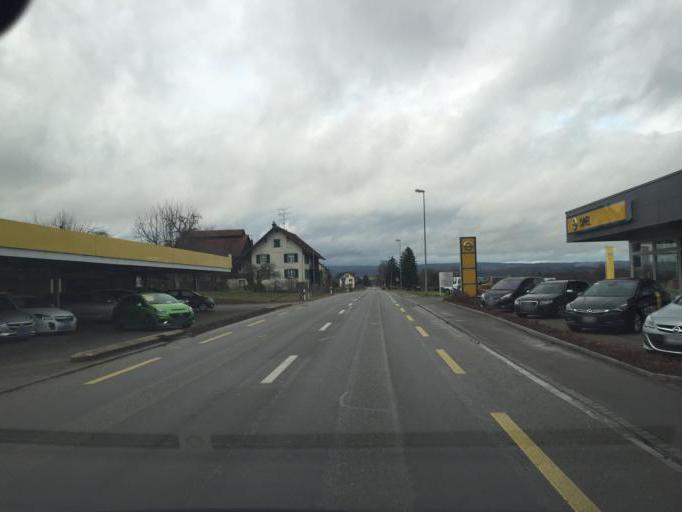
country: DE
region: Baden-Wuerttemberg
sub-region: Freiburg Region
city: Busingen
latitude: 47.6652
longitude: 8.7005
